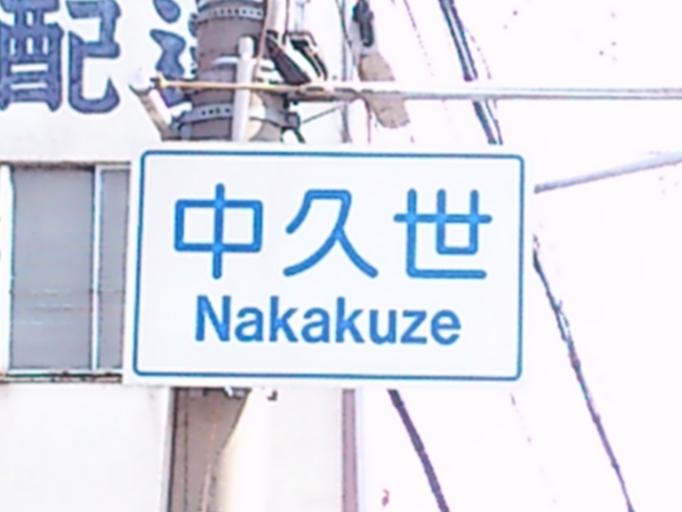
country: JP
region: Kyoto
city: Muko
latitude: 34.9592
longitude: 135.7170
